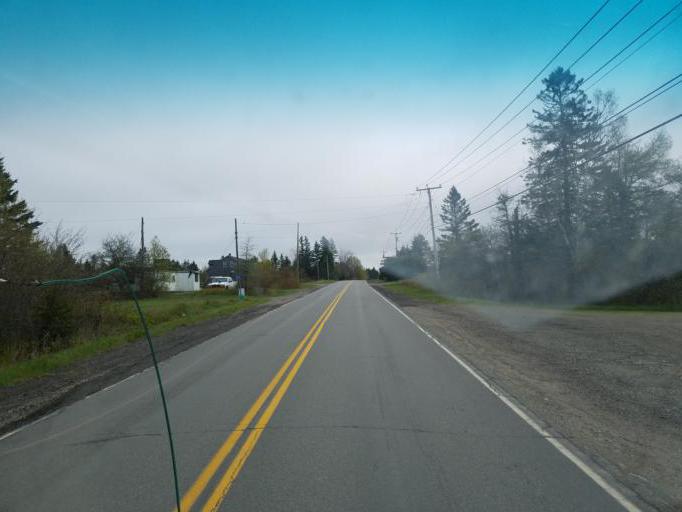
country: US
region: Maine
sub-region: Washington County
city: Eastport
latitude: 44.8235
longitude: -67.0473
